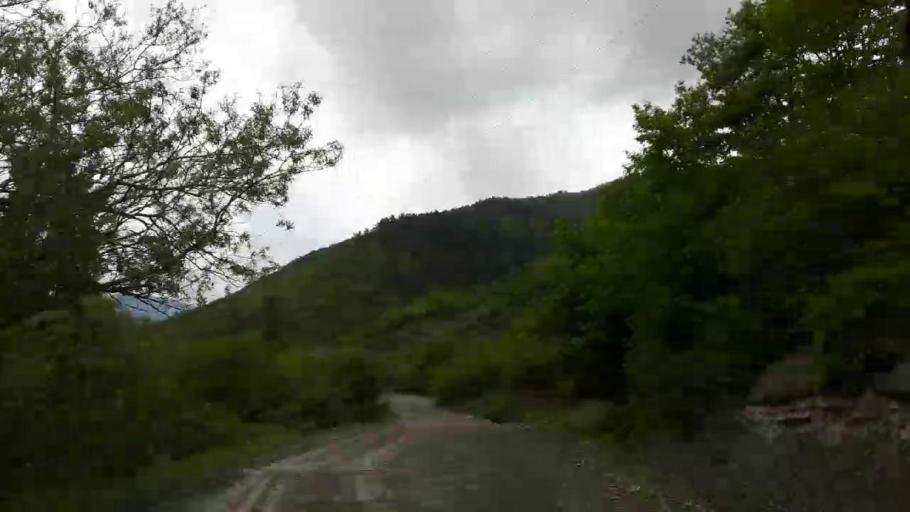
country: GE
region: Shida Kartli
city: Gori
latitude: 41.8791
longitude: 43.9921
